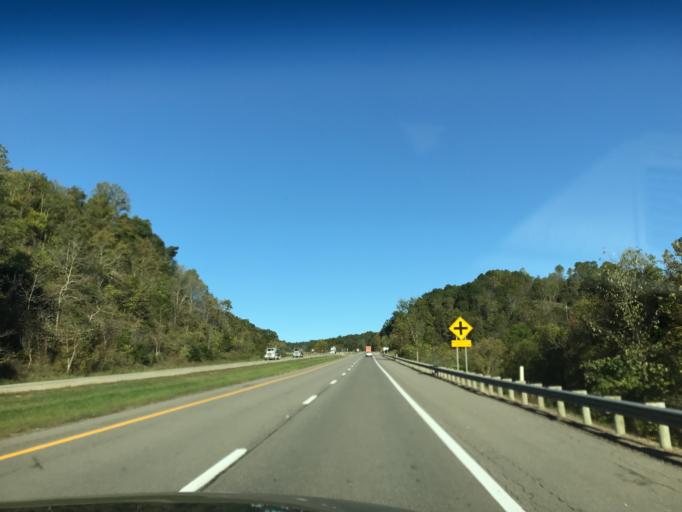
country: US
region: Ohio
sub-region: Washington County
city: Newport
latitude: 39.2493
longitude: -81.2430
